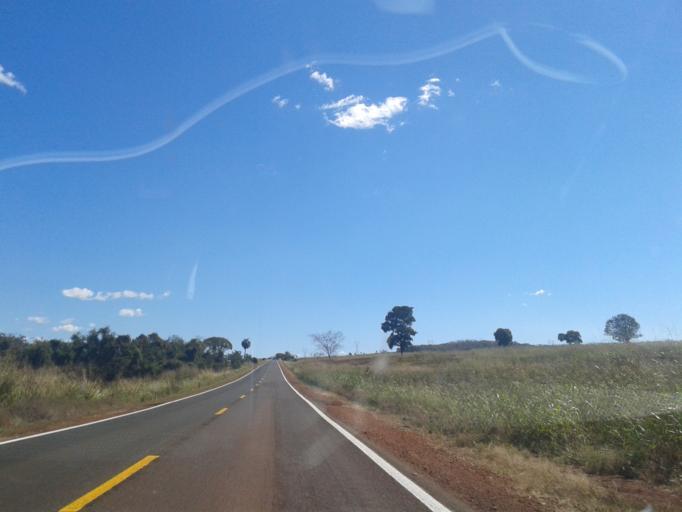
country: BR
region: Minas Gerais
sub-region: Capinopolis
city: Capinopolis
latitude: -18.6900
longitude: -49.4298
